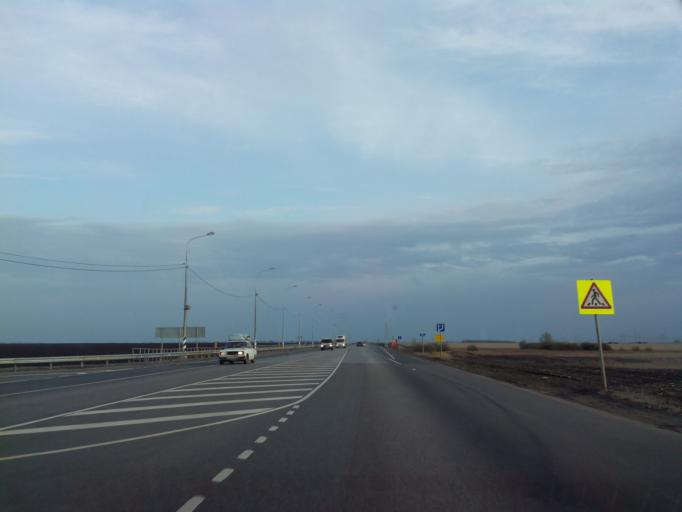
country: RU
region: Rjazan
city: Ryazhsk
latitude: 53.5790
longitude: 40.0431
